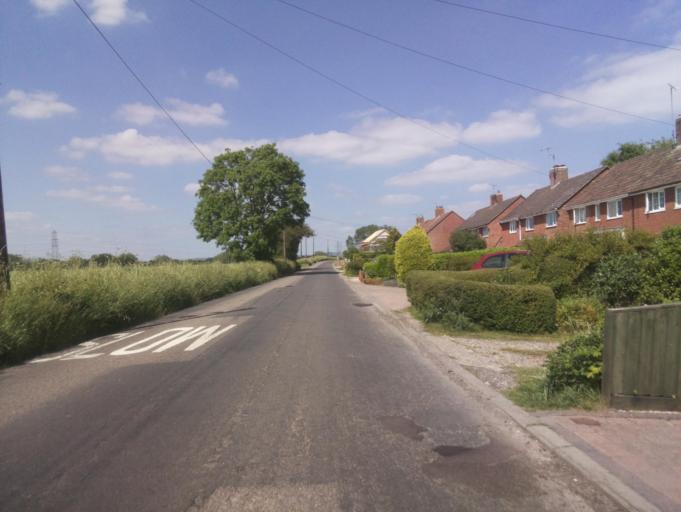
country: GB
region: England
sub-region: Wiltshire
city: Rushall
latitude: 51.3098
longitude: -1.8144
